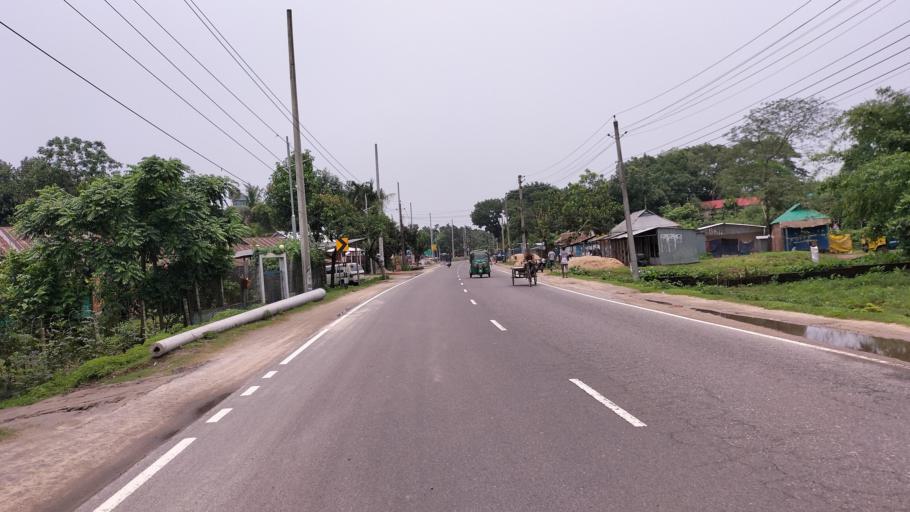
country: BD
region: Dhaka
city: Mymensingh
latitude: 24.7714
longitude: 90.4566
